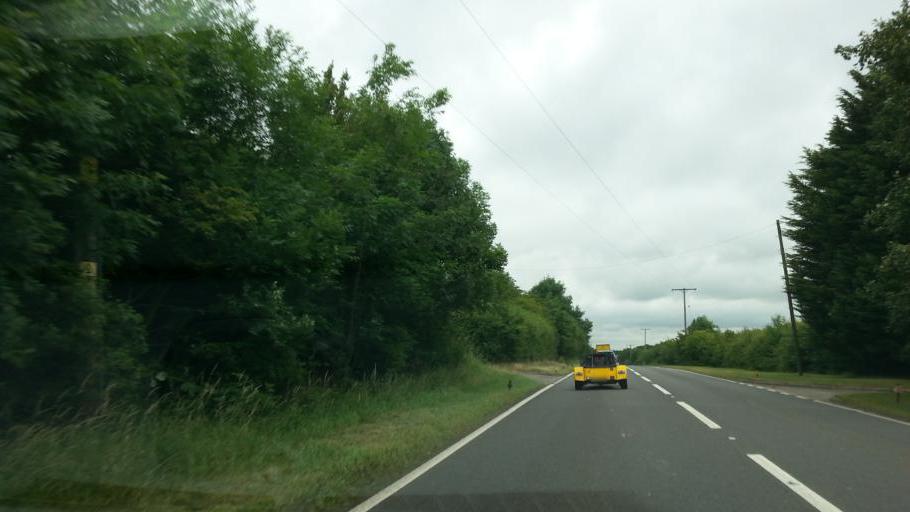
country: GB
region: England
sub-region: District of Rutland
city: South Luffenham
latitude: 52.5701
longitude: -0.5706
